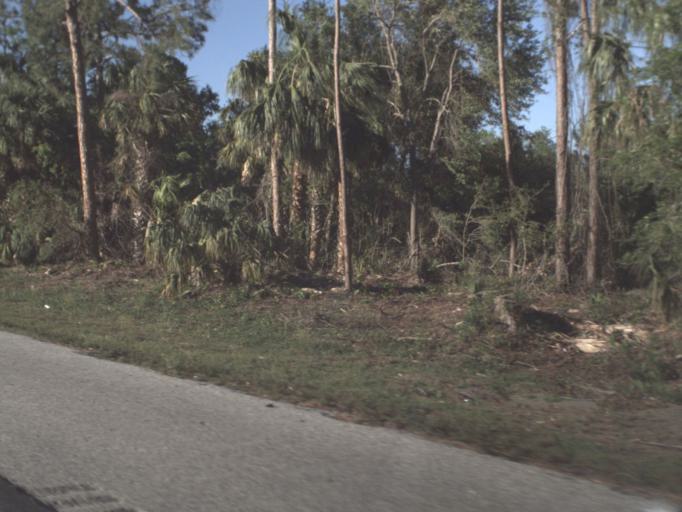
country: US
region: Florida
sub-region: Flagler County
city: Flagler Beach
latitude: 29.4464
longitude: -81.1724
